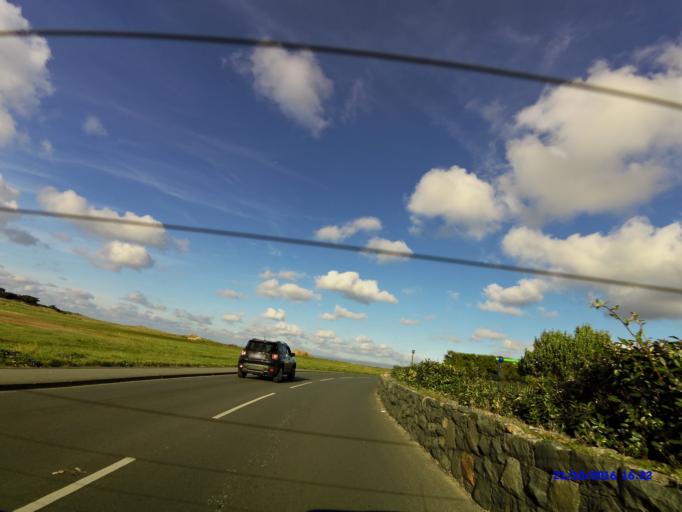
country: GG
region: St Peter Port
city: Saint Peter Port
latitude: 49.4713
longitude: -2.6054
